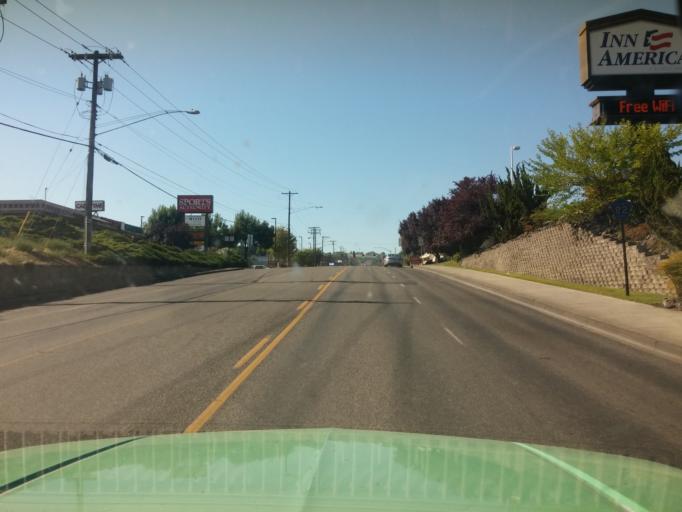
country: US
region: Idaho
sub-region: Nez Perce County
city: Lewiston
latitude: 46.4143
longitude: -117.0020
